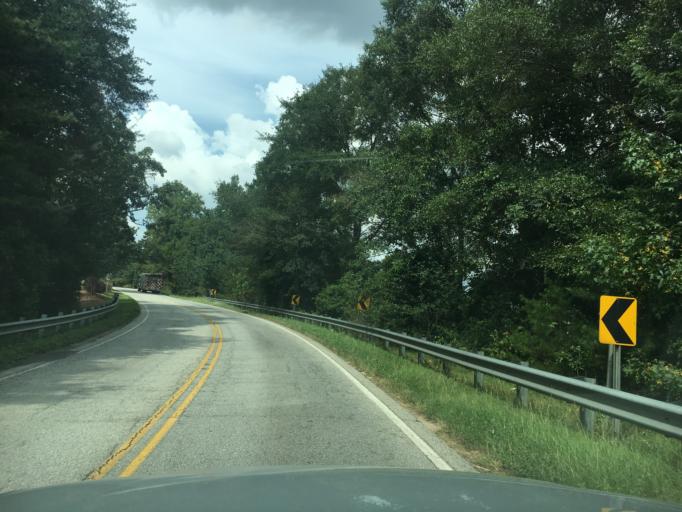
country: US
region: South Carolina
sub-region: Greenville County
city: Five Forks
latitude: 34.8457
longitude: -82.2251
